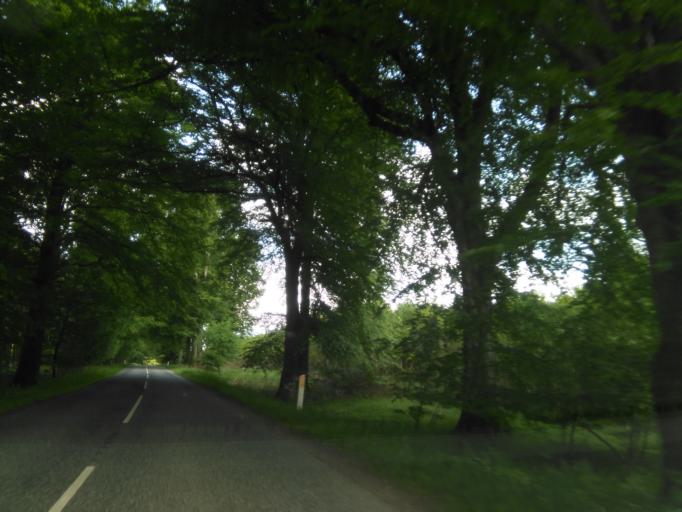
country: DK
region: Central Jutland
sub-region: Favrskov Kommune
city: Hammel
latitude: 56.2399
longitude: 9.9331
